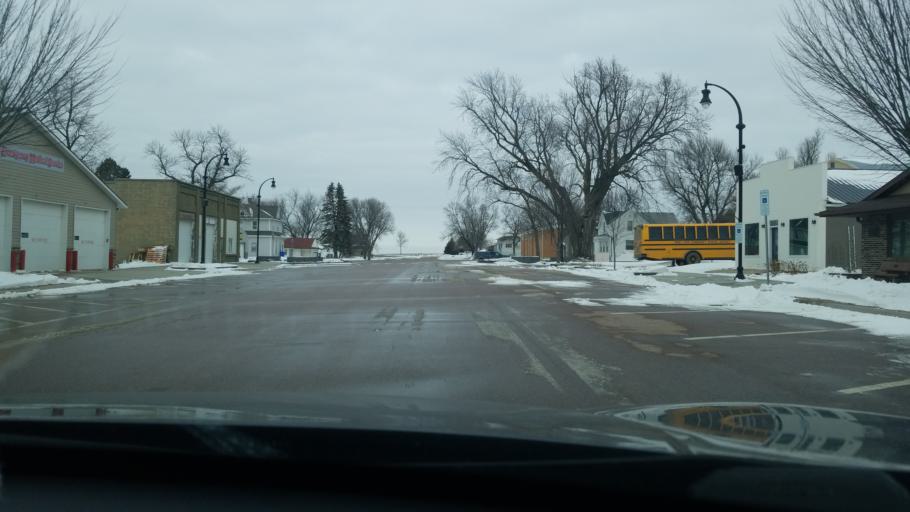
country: US
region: South Dakota
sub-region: Minnehaha County
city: Brandon
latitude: 43.4540
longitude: -96.4342
